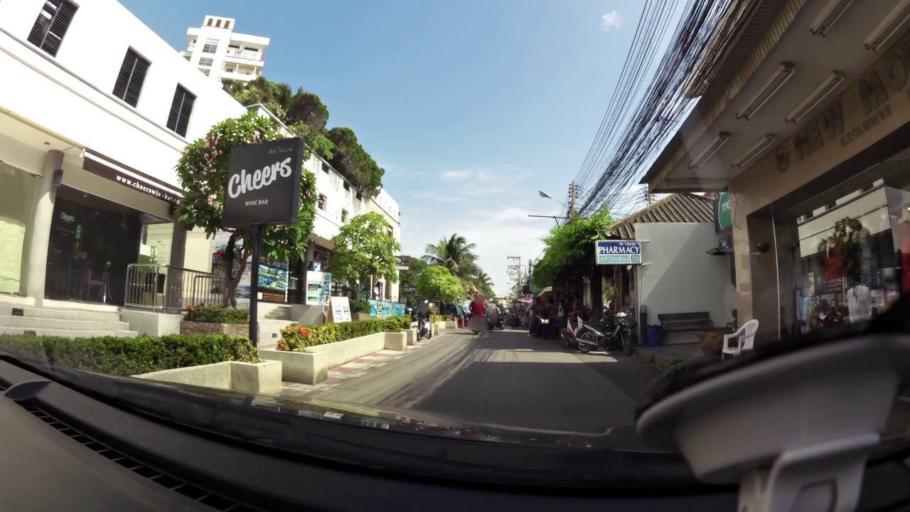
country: TH
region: Prachuap Khiri Khan
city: Hua Hin
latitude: 12.5714
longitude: 99.9602
